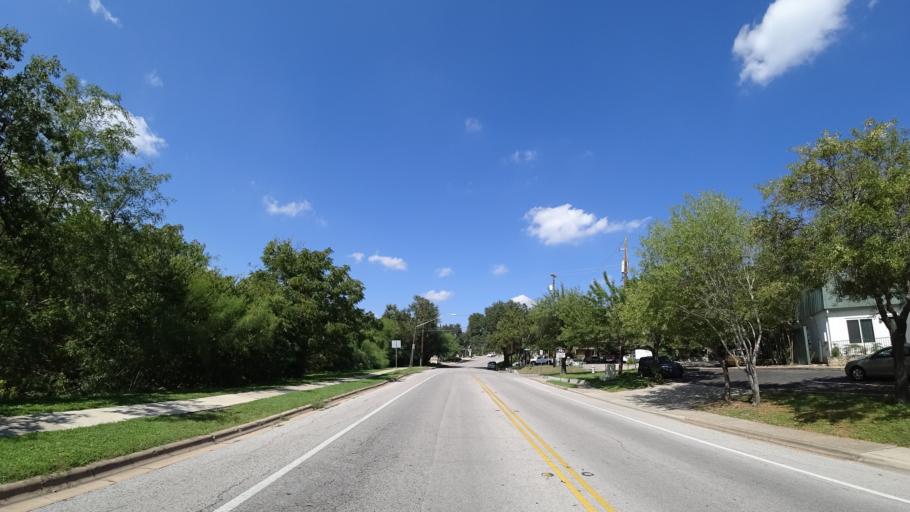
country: US
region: Texas
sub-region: Travis County
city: Austin
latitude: 30.3097
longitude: -97.7485
